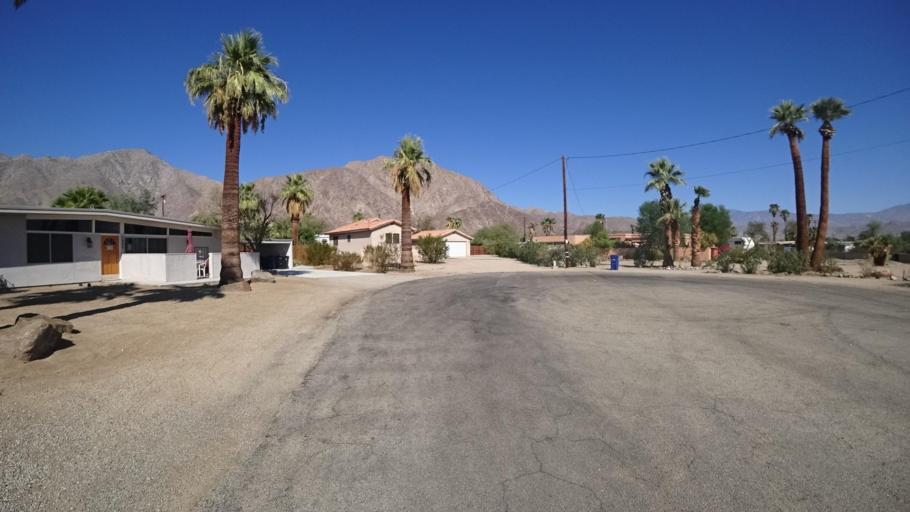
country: US
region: California
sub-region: San Diego County
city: Borrego Springs
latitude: 33.2744
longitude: -116.3917
